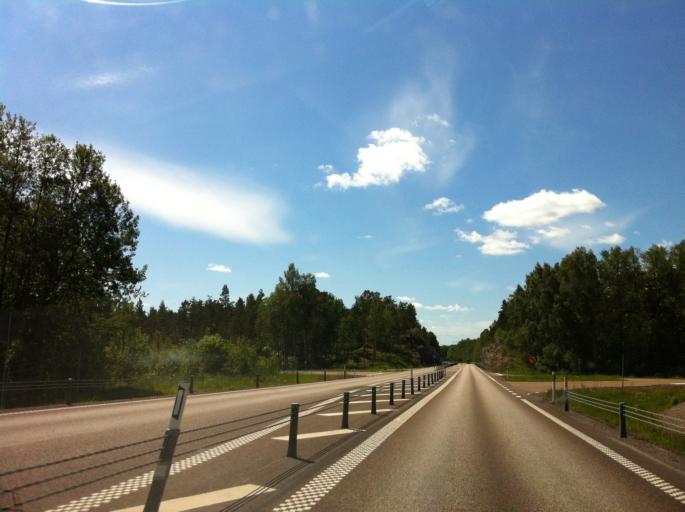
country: SE
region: Vaestra Goetaland
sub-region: Melleruds Kommun
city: Mellerud
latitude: 58.8019
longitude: 12.5261
